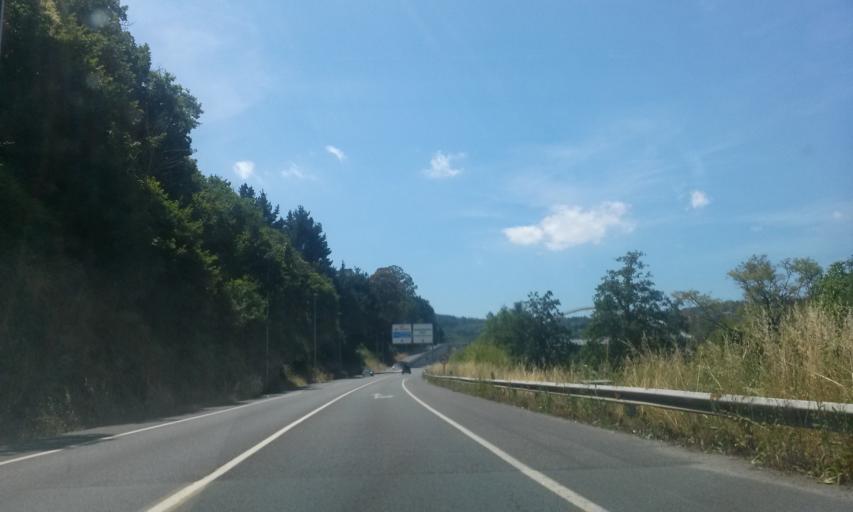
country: ES
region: Galicia
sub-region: Provincia de Lugo
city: Lugo
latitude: 43.0002
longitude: -7.5601
